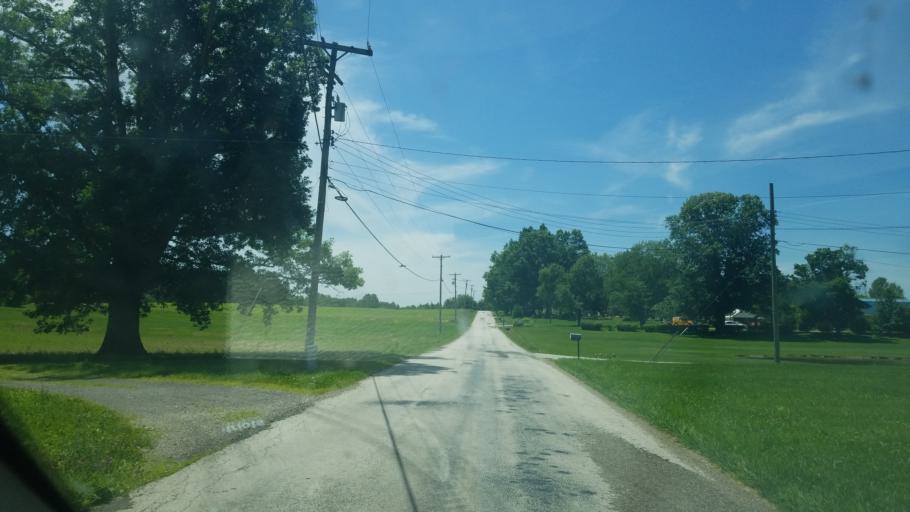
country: US
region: Ohio
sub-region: Stark County
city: Alliance
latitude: 40.8578
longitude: -81.0816
